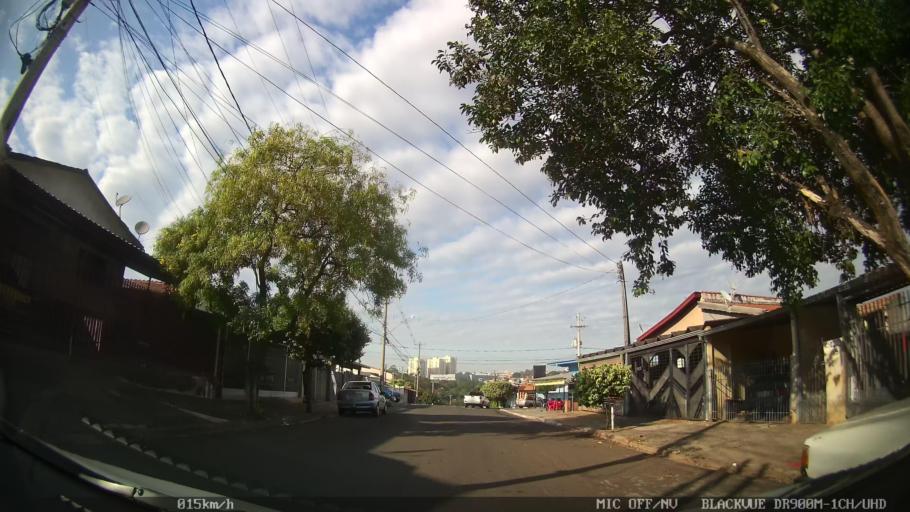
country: BR
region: Sao Paulo
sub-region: Americana
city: Americana
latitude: -22.7283
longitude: -47.3747
